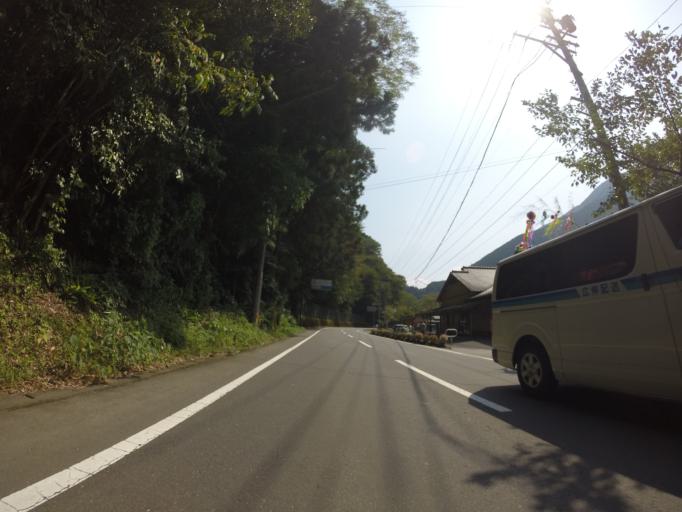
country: JP
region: Shizuoka
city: Shizuoka-shi
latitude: 35.1414
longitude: 138.3663
